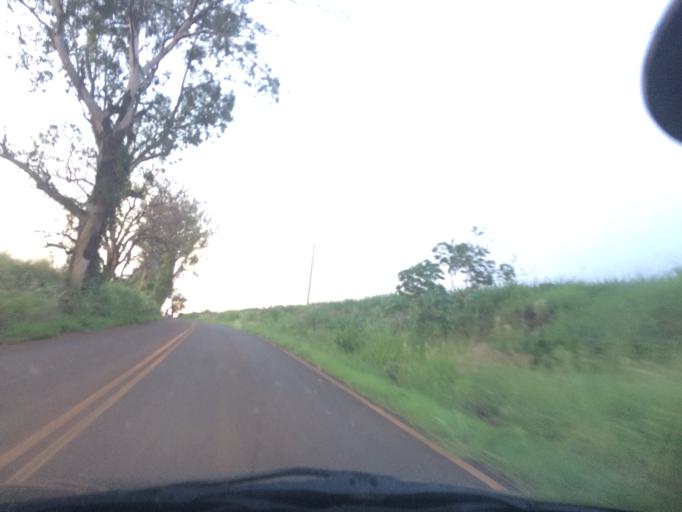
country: BR
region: Sao Paulo
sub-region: Tambau
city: Tambau
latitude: -21.7078
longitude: -47.1995
